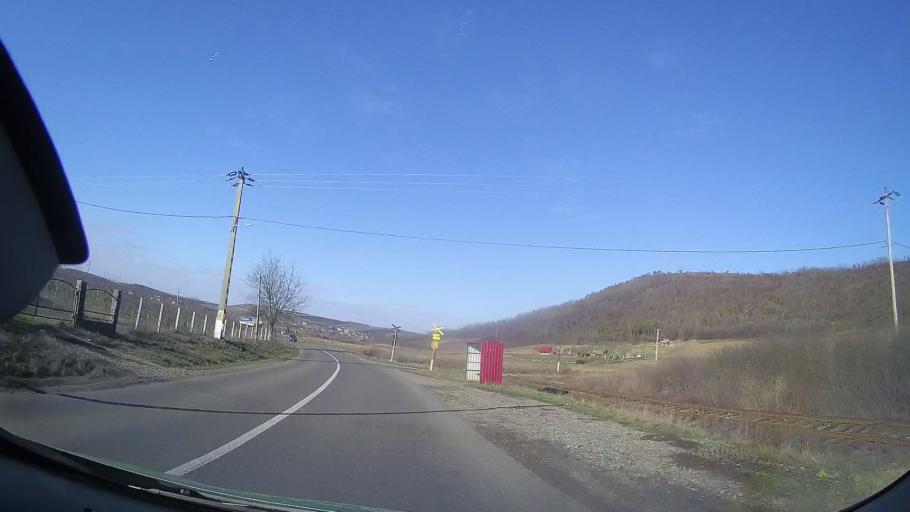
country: RO
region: Mures
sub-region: Comuna Mihesu de Campie
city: Mihesu de Campie
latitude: 46.6702
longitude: 24.1723
